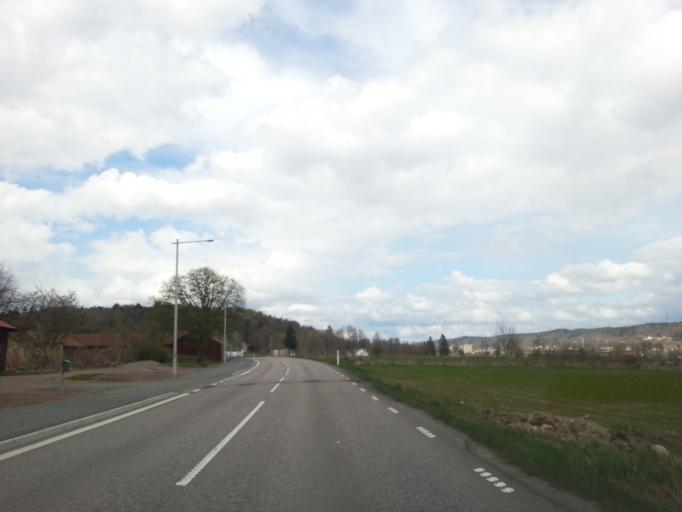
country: SE
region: Vaestra Goetaland
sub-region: Ale Kommun
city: Surte
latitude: 57.8069
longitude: 11.9970
